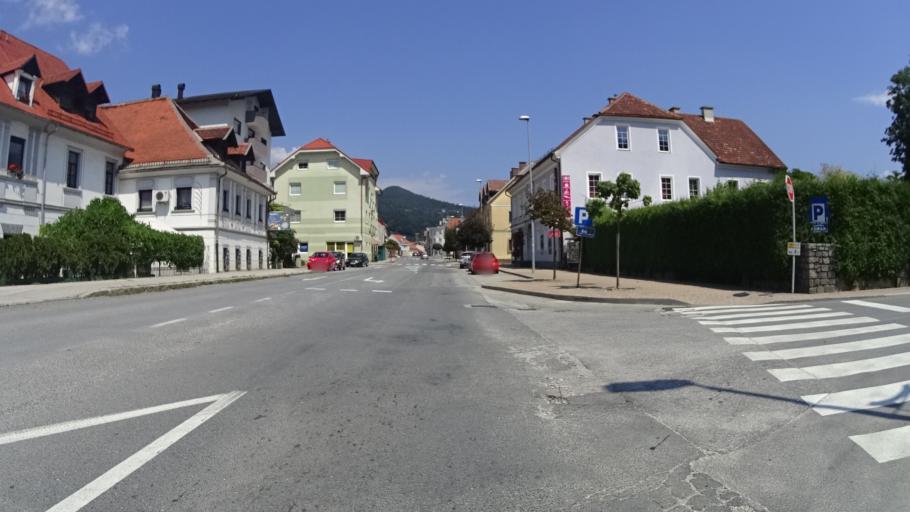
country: SI
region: Prevalje
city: Prevalje
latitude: 46.5447
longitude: 14.9142
